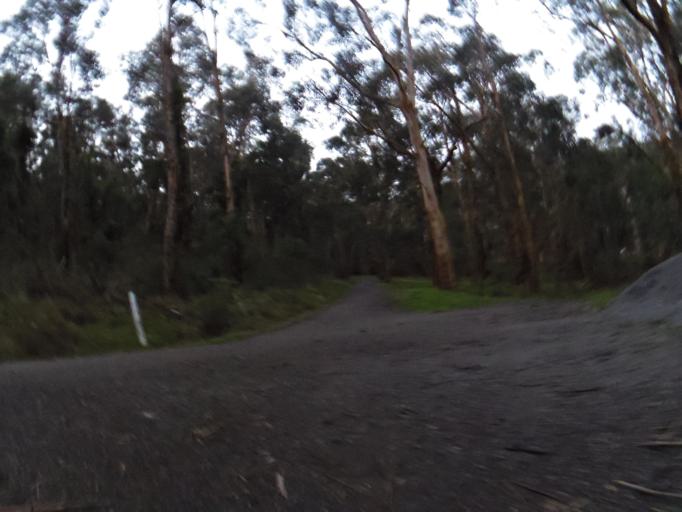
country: AU
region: Victoria
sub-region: Yarra Ranges
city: Tremont
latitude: -37.8917
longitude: 145.3152
